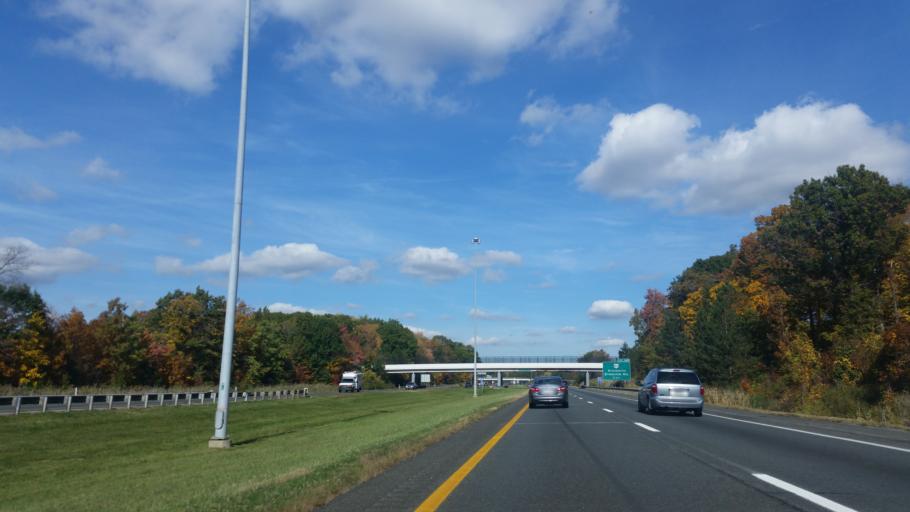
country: US
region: Ohio
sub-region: Cuyahoga County
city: Brecksville
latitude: 41.2809
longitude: -81.6361
